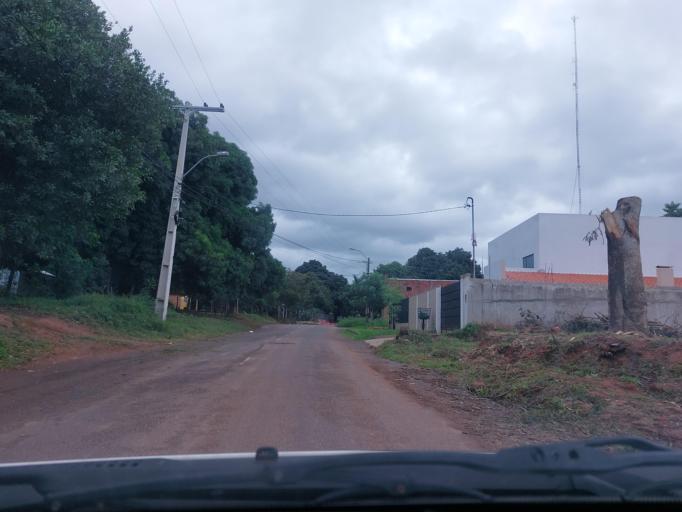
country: PY
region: San Pedro
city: Guayaybi
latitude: -24.6795
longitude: -56.4502
